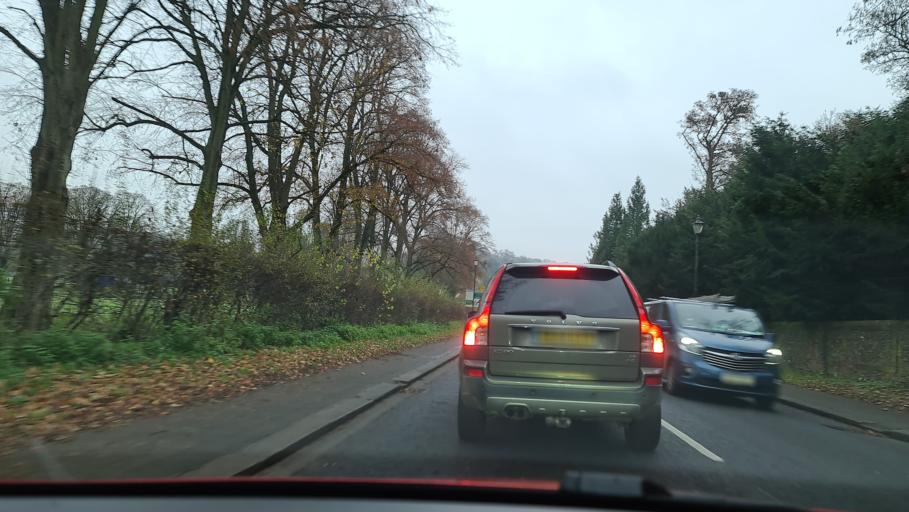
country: GB
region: England
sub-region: Buckinghamshire
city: High Wycombe
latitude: 51.6447
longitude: -0.7986
